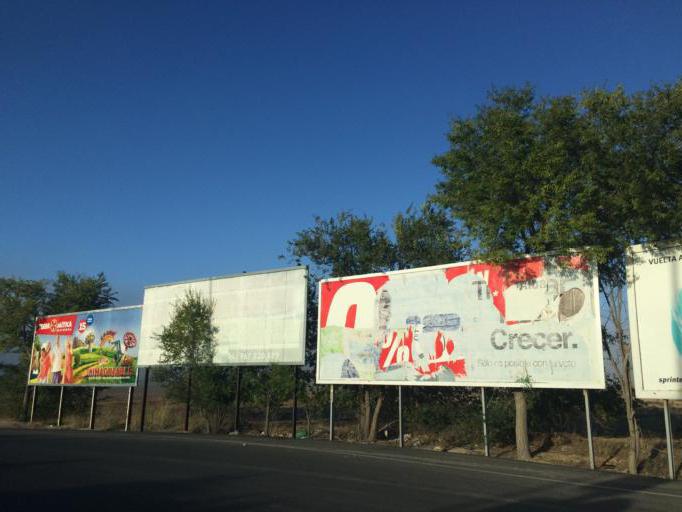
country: ES
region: Castille-La Mancha
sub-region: Provincia de Albacete
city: Albacete
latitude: 39.0086
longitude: -1.8891
